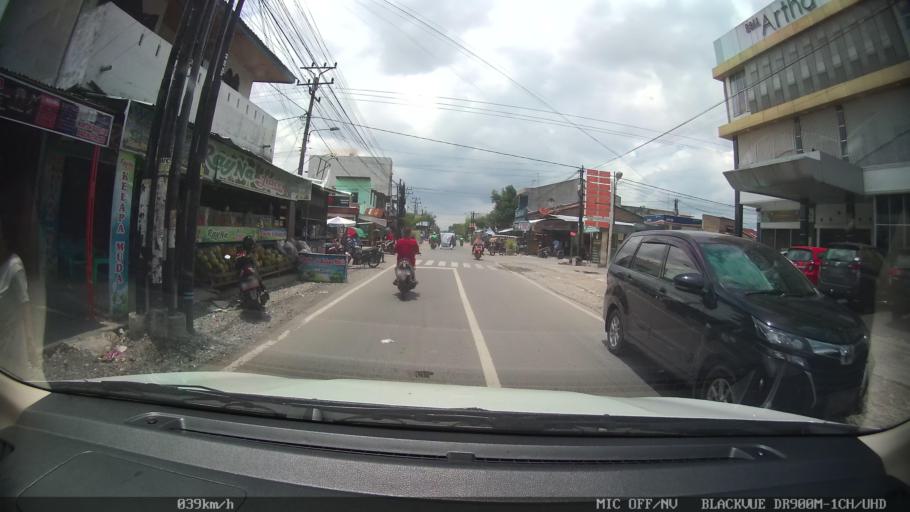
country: ID
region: North Sumatra
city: Medan
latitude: 3.6162
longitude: 98.6915
